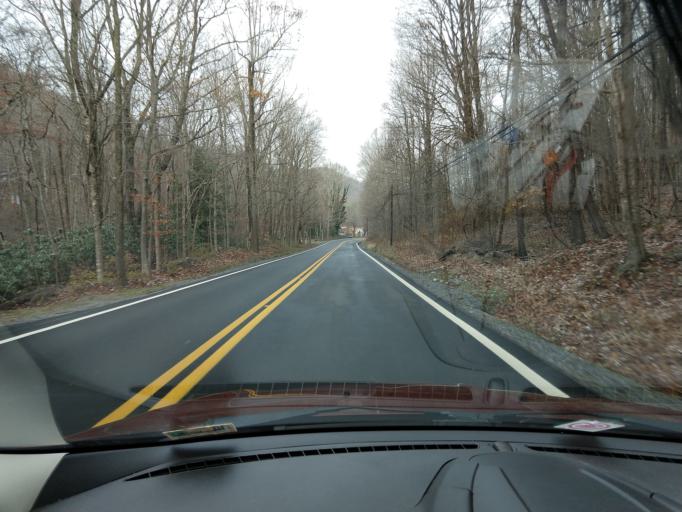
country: US
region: West Virginia
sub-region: Nicholas County
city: Richwood
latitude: 38.1399
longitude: -80.6861
